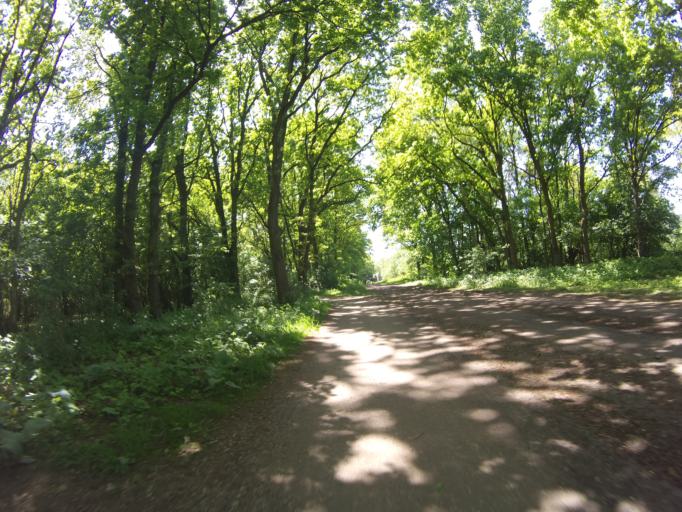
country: NL
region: North Holland
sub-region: Gemeente Hilversum
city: Hilversum
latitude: 52.2470
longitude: 5.1737
